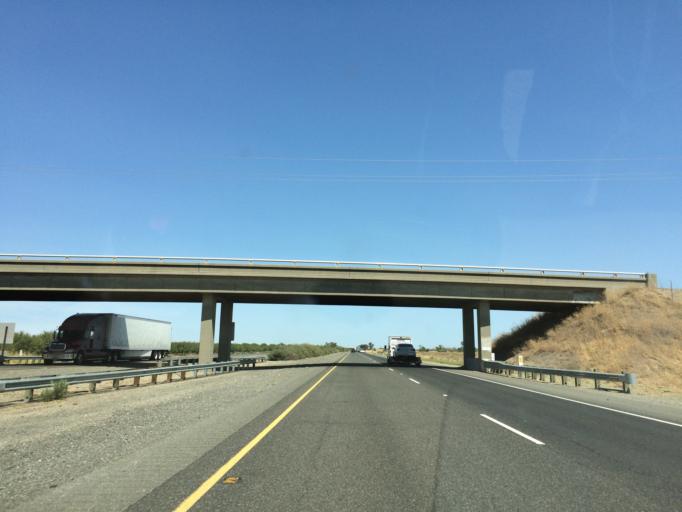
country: US
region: California
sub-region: Glenn County
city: Willows
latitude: 39.6107
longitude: -122.2073
